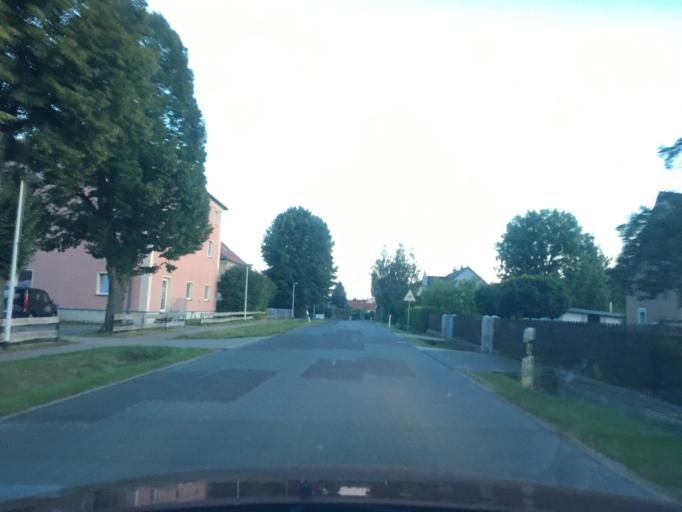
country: PL
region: Lower Silesian Voivodeship
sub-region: Powiat zgorzelecki
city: Piensk
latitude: 51.2344
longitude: 15.0107
